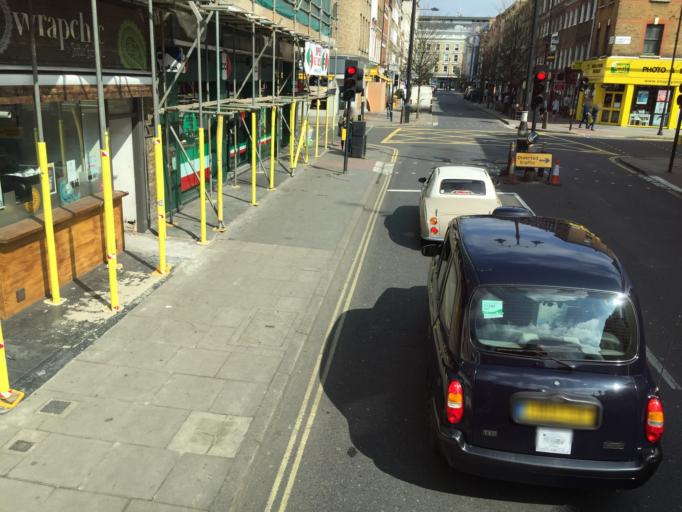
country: GB
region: England
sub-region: Greater London
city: London
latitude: 51.5193
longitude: -0.1361
